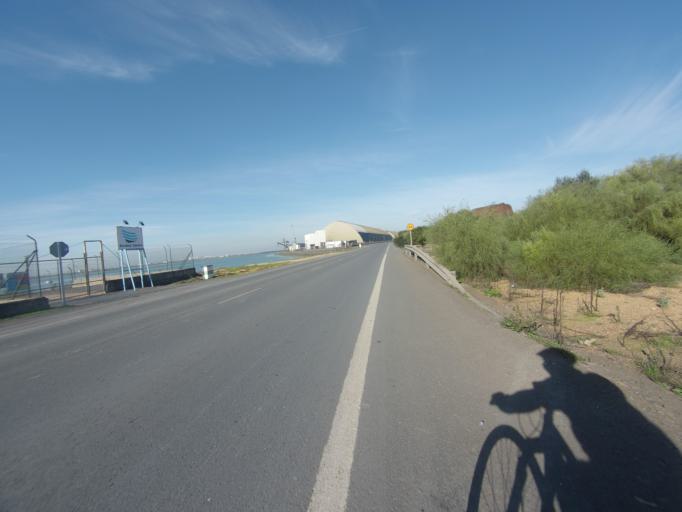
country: ES
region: Andalusia
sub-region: Provincia de Huelva
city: Punta Umbria
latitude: 37.1784
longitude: -6.9184
